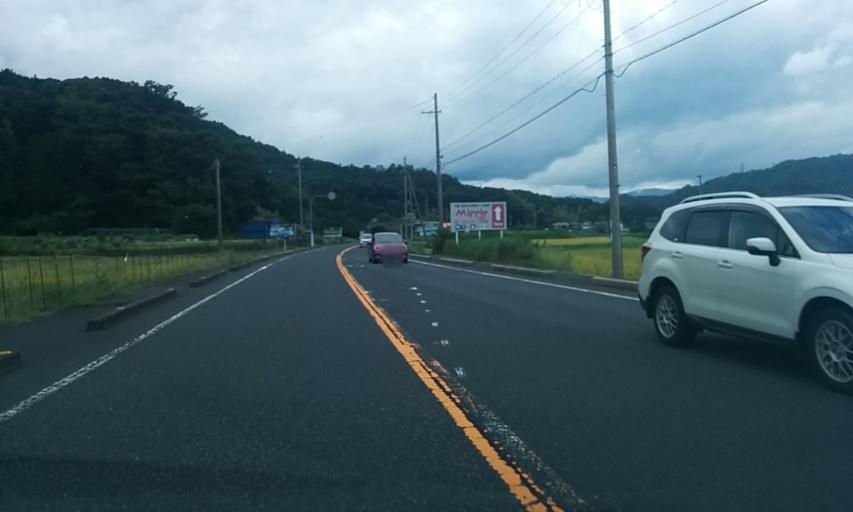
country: JP
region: Kyoto
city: Miyazu
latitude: 35.5400
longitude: 135.2360
